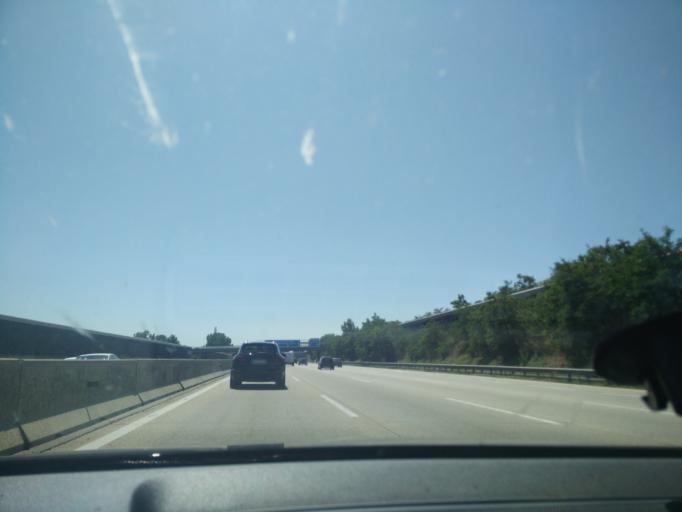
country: AT
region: Lower Austria
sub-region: Politischer Bezirk Modling
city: Biedermannsdorf
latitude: 48.0866
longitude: 16.3306
